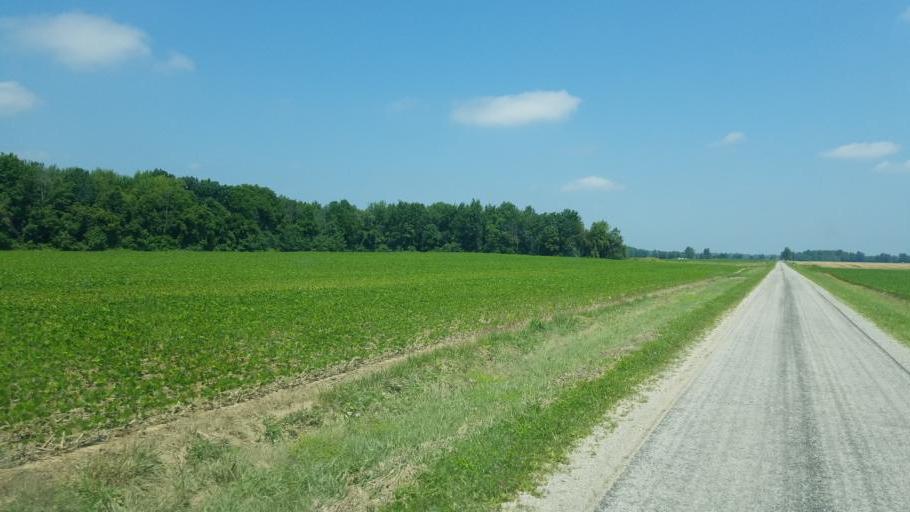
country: US
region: Ohio
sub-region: Crawford County
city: Bucyrus
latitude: 41.0125
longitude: -82.9775
